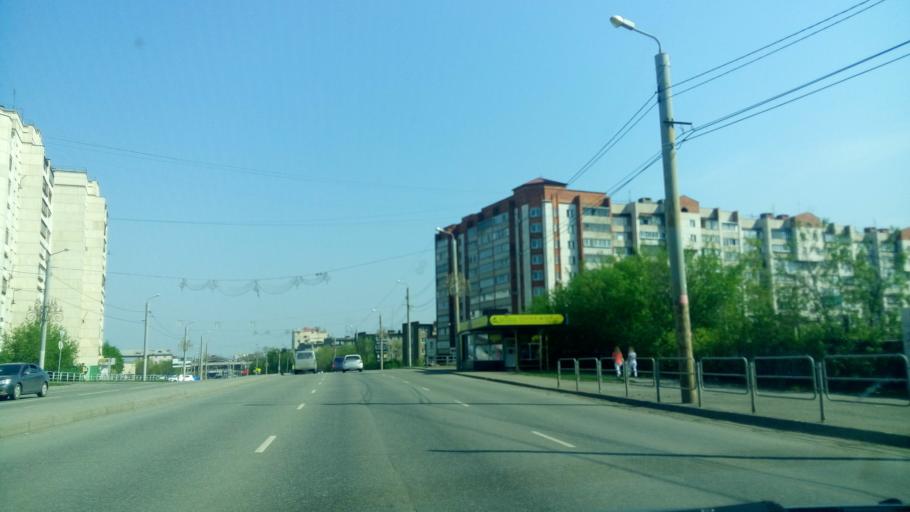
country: RU
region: Chelyabinsk
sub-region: Gorod Chelyabinsk
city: Chelyabinsk
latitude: 55.1439
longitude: 61.4049
